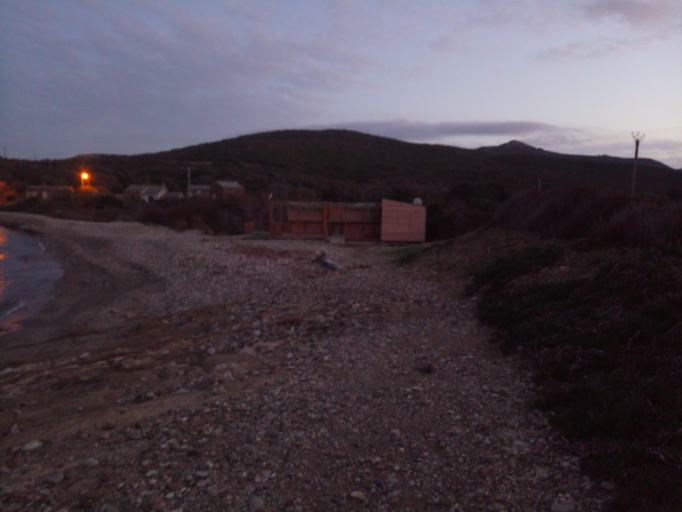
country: FR
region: Corsica
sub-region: Departement de la Haute-Corse
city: Brando
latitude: 43.0070
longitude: 9.3887
